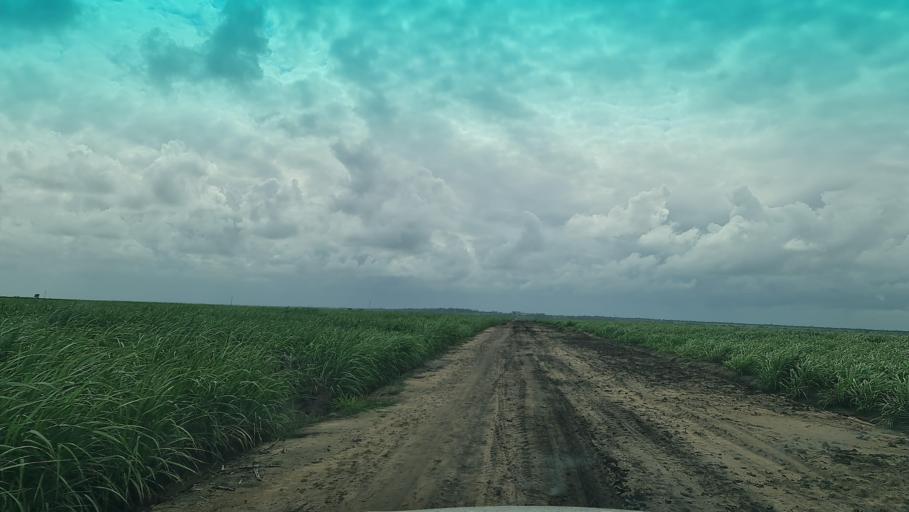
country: MZ
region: Maputo
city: Manhica
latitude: -25.4535
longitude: 32.8331
